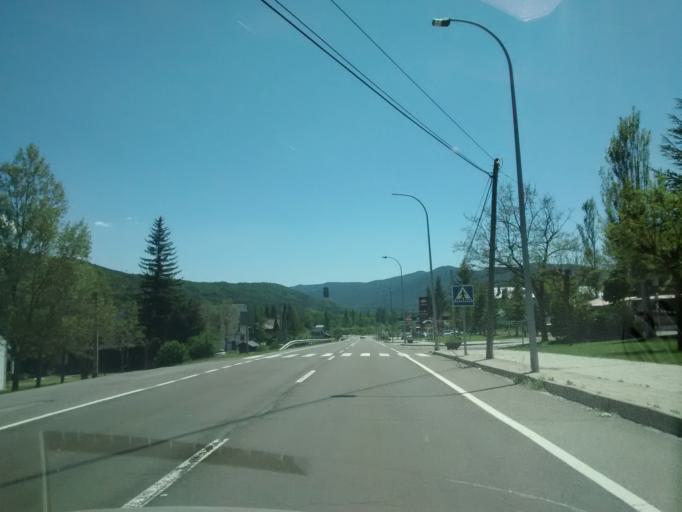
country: ES
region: Aragon
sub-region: Provincia de Huesca
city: Villanua
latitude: 42.6793
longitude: -0.5372
